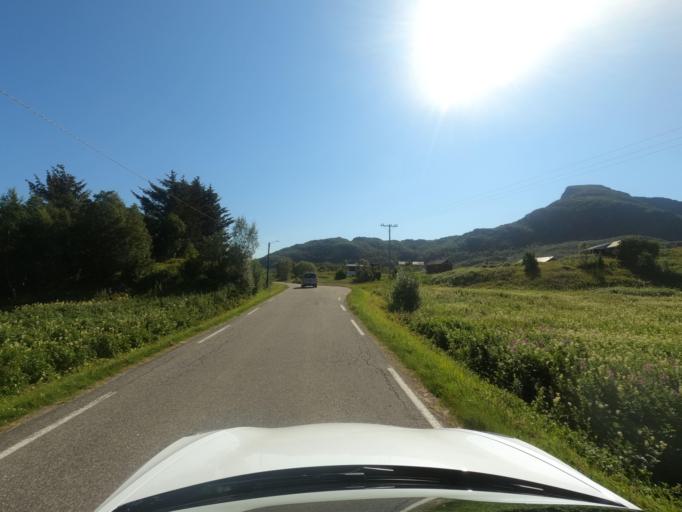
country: NO
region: Nordland
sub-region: Hadsel
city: Stokmarknes
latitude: 68.3032
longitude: 15.0149
